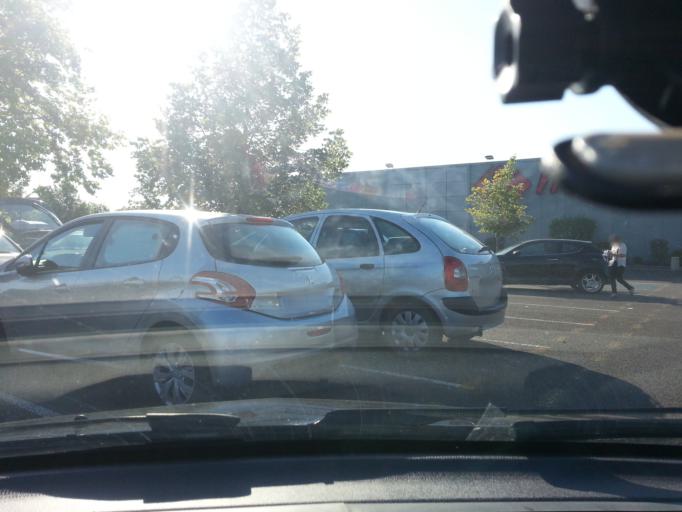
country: FR
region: Bourgogne
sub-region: Departement de Saone-et-Loire
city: Saint-Marcel
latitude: 46.7779
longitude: 4.8968
